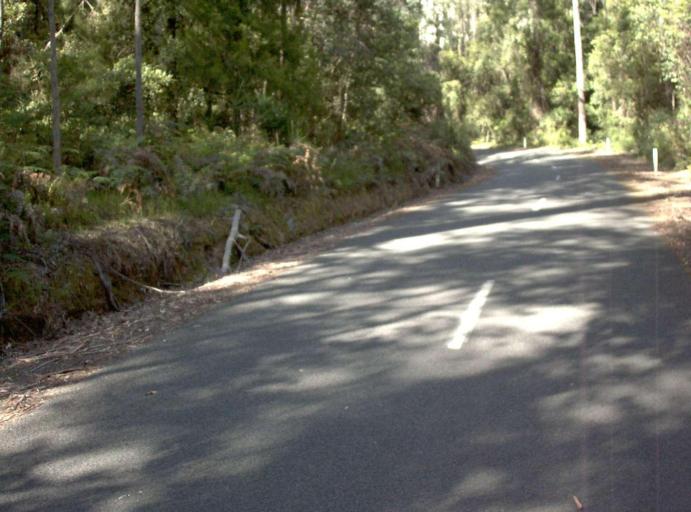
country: AU
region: Victoria
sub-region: East Gippsland
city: Lakes Entrance
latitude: -37.4452
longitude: 148.5836
